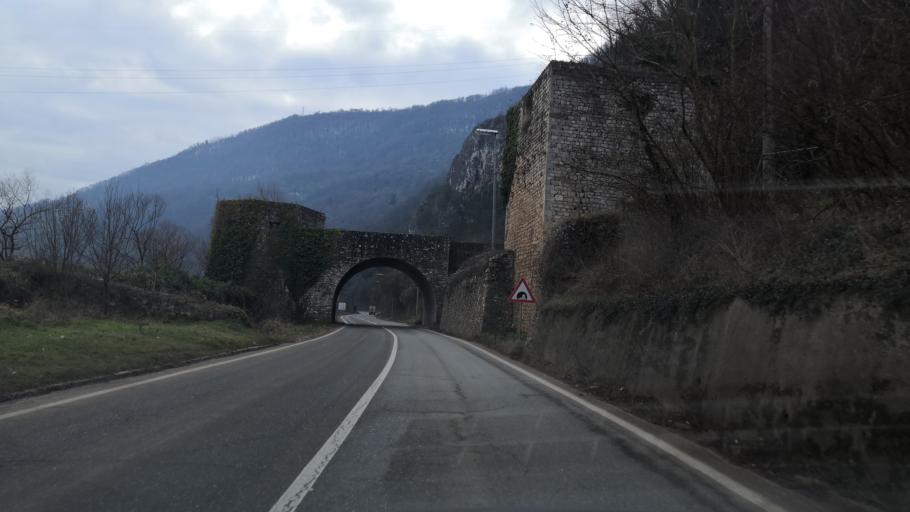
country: RS
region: Central Serbia
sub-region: Macvanski Okrug
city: Mali Zvornik
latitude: 44.3750
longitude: 19.1018
